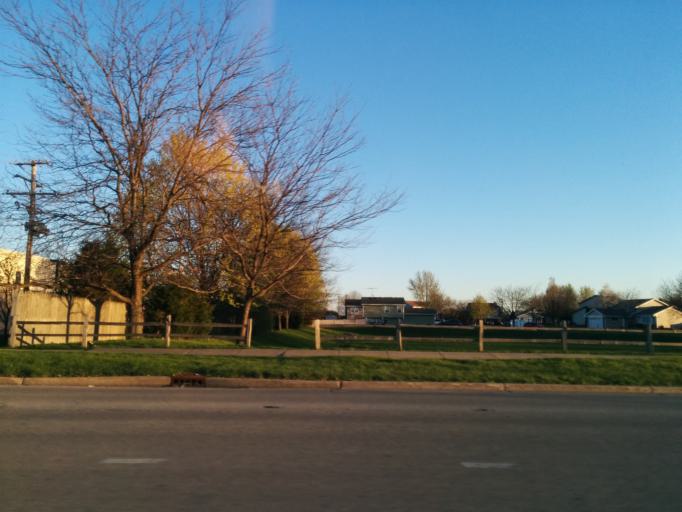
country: US
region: Illinois
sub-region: DuPage County
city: Hanover Park
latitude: 41.9738
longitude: -88.1516
